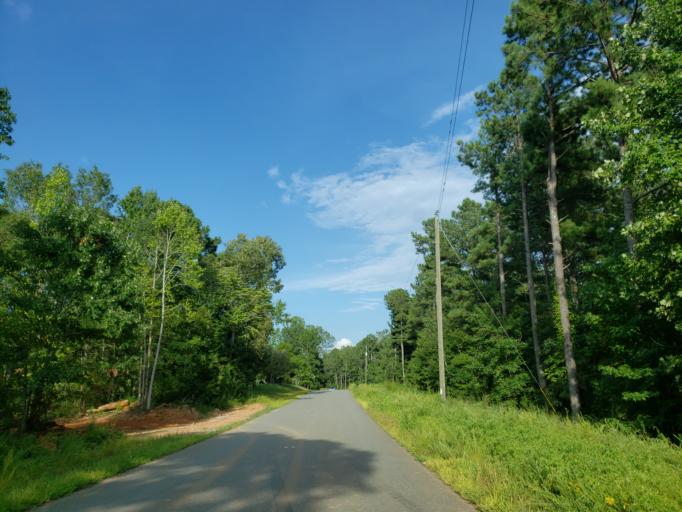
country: US
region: Georgia
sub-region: Bartow County
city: Emerson
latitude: 34.1908
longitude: -84.6518
